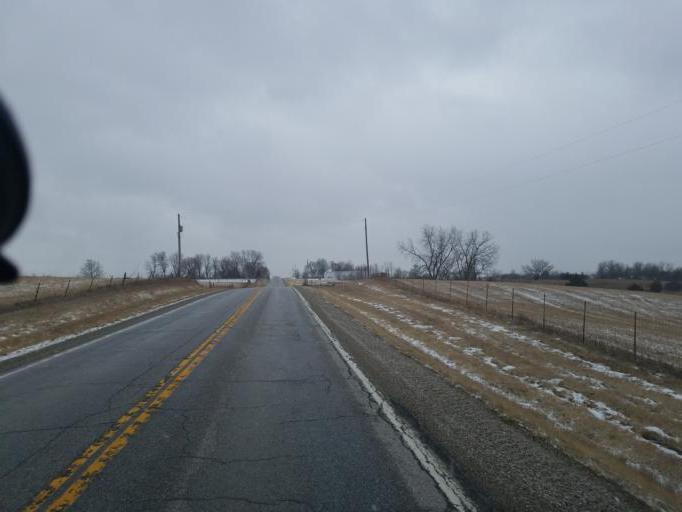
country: US
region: Missouri
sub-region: Putnam County
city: Unionville
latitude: 40.5137
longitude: -93.0094
